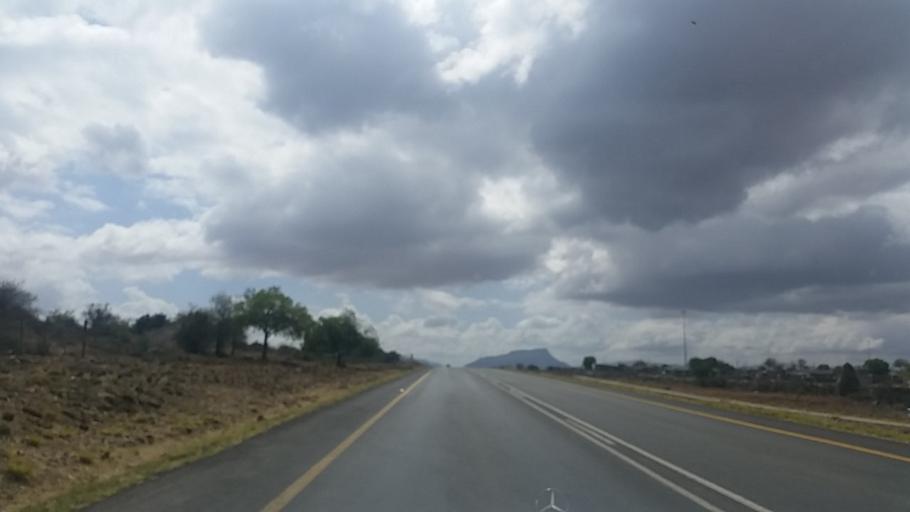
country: ZA
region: Eastern Cape
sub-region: Cacadu District Municipality
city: Graaff-Reinet
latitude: -32.2384
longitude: 24.5360
